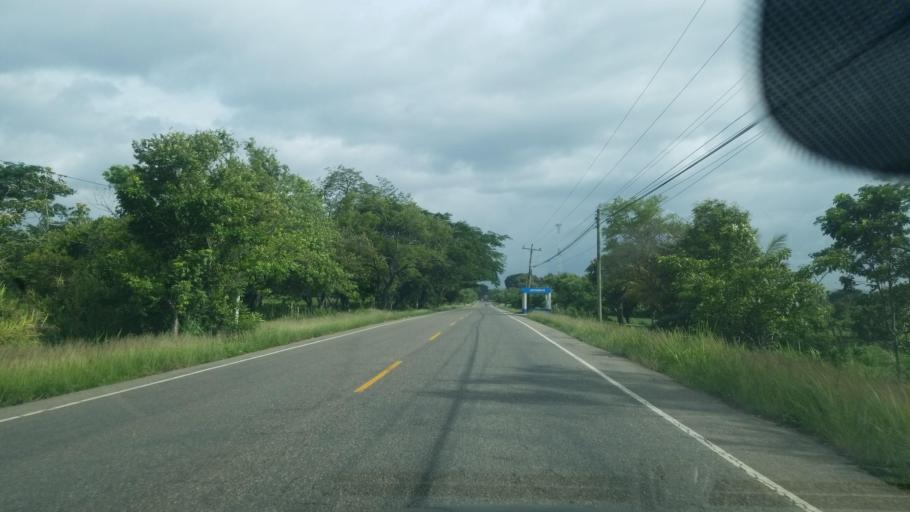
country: HN
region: Ocotepeque
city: Santa Lucia
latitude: 14.4095
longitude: -89.1951
